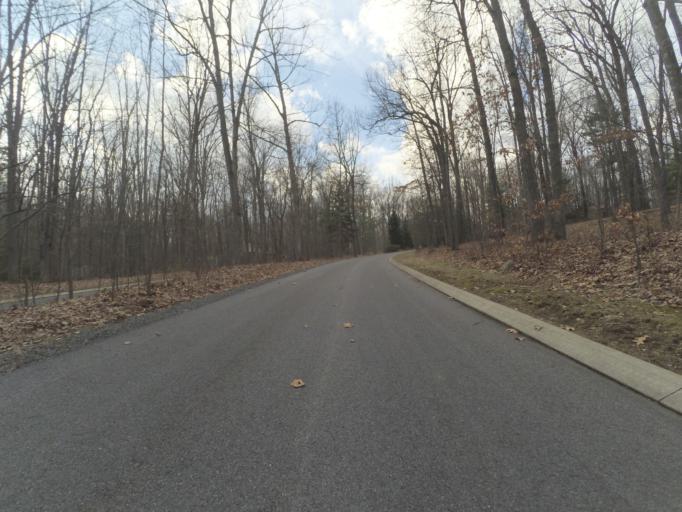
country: US
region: Pennsylvania
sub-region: Centre County
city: Park Forest Village
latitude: 40.7903
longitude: -77.9204
